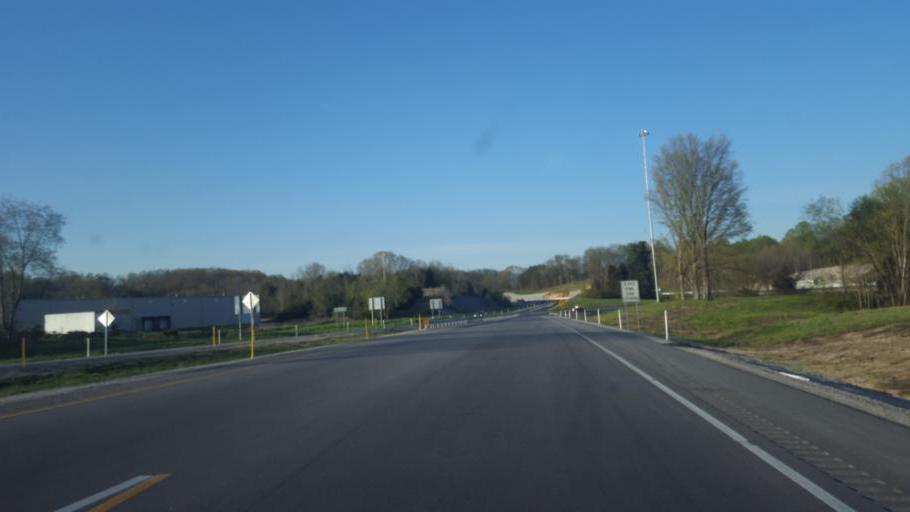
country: US
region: Kentucky
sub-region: Hart County
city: Munfordville
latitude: 37.2938
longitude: -85.9046
